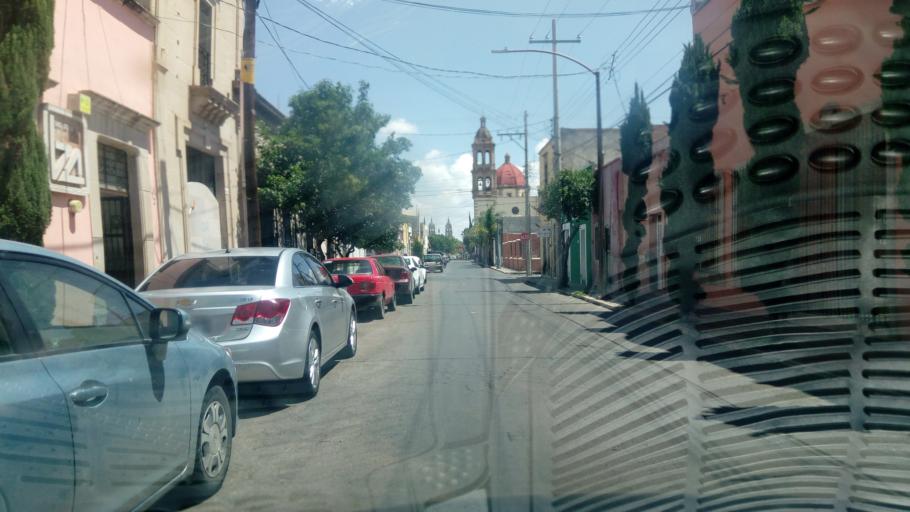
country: MX
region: Durango
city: Victoria de Durango
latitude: 24.0319
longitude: -104.6712
